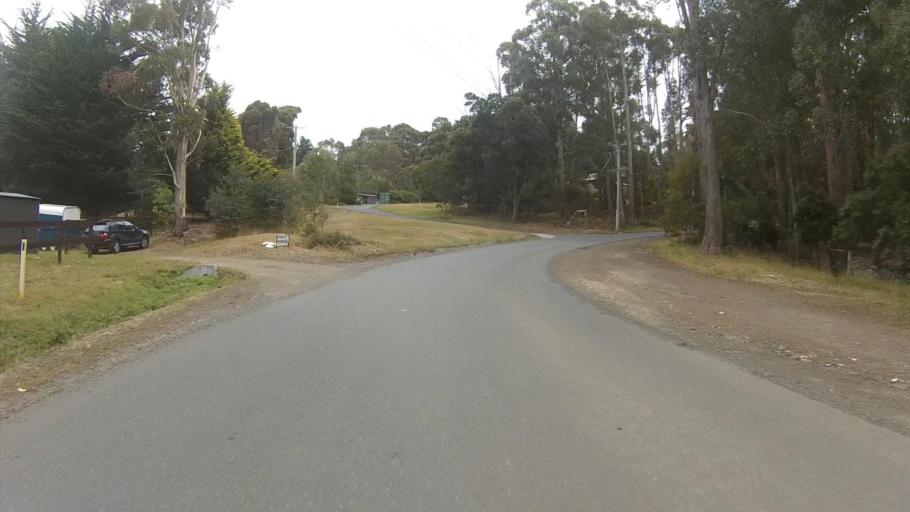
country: AU
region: Tasmania
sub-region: Kingborough
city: Kingston
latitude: -42.9635
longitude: 147.2772
